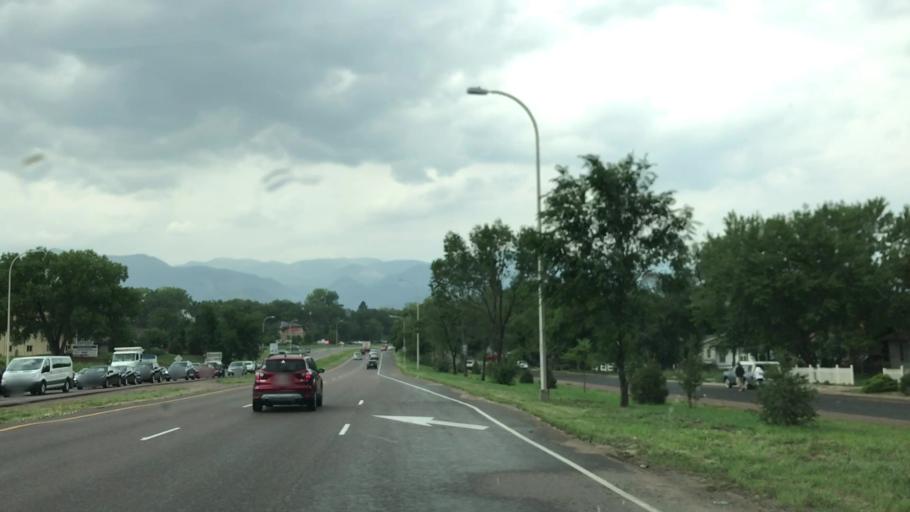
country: US
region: Colorado
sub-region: El Paso County
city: Stratmoor
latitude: 38.7958
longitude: -104.8041
